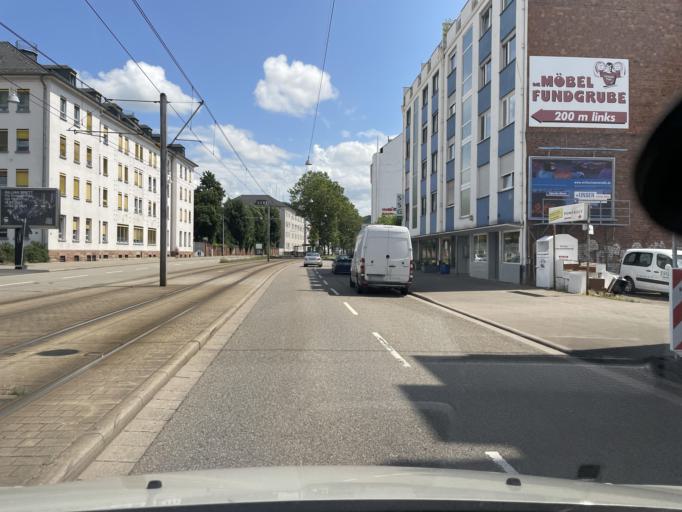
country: DE
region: Saarland
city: Saarbrucken
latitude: 49.2287
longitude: 7.0145
